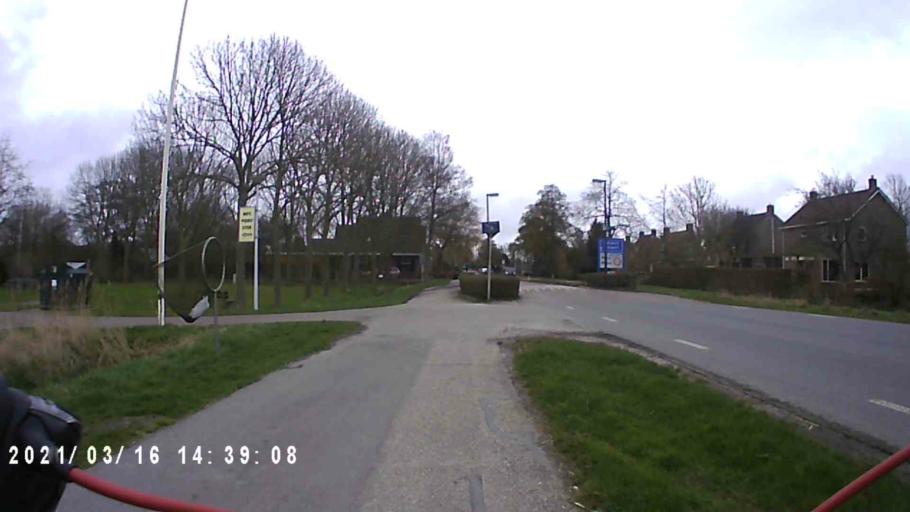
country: NL
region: Friesland
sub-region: Gemeente Harlingen
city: Harlingen
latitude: 53.1421
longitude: 5.4343
